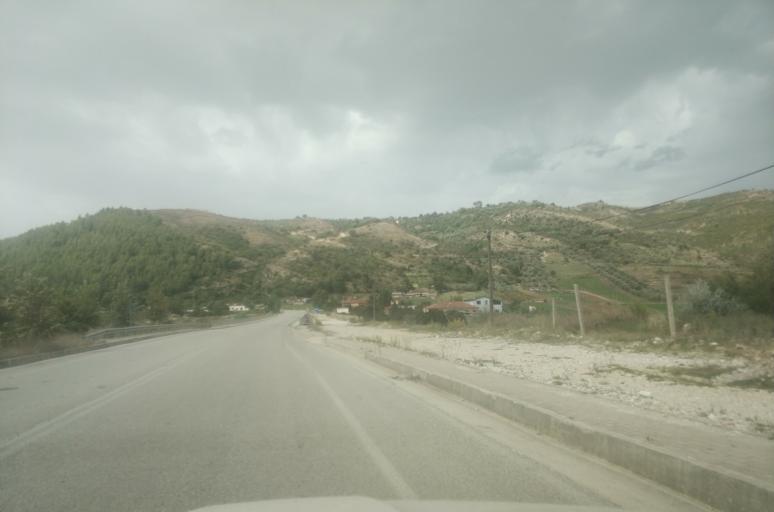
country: AL
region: Gjirokaster
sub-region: Rrethi i Tepelenes
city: Memaliaj
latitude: 40.3502
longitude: 19.9740
